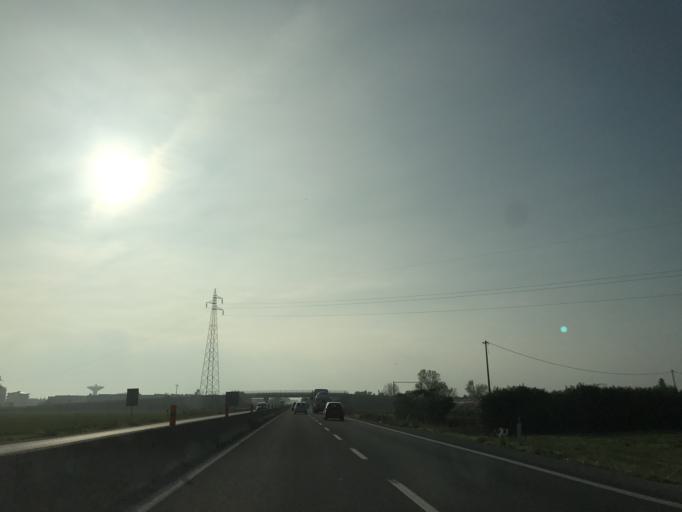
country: IT
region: Emilia-Romagna
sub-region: Provincia di Rimini
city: Bellaria-Igea Marina
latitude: 44.1357
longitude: 12.4626
